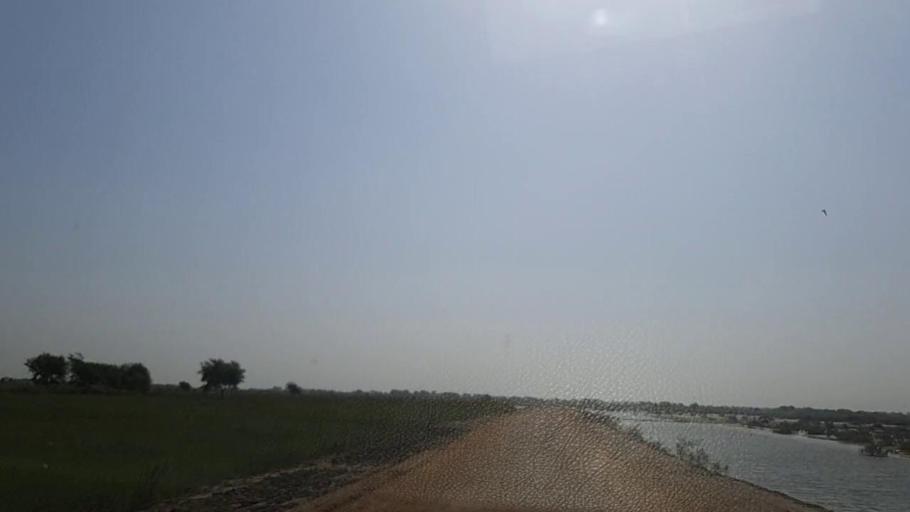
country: PK
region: Sindh
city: Daro Mehar
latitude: 24.7061
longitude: 68.1264
